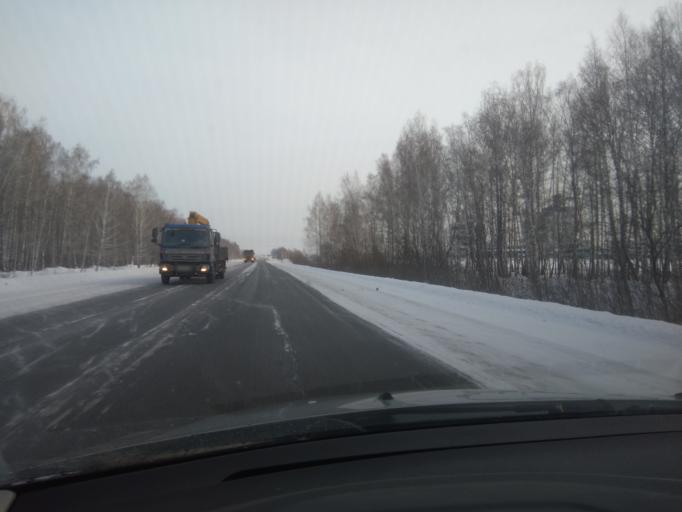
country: RU
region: Sverdlovsk
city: Bogdanovich
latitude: 56.8053
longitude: 62.0286
